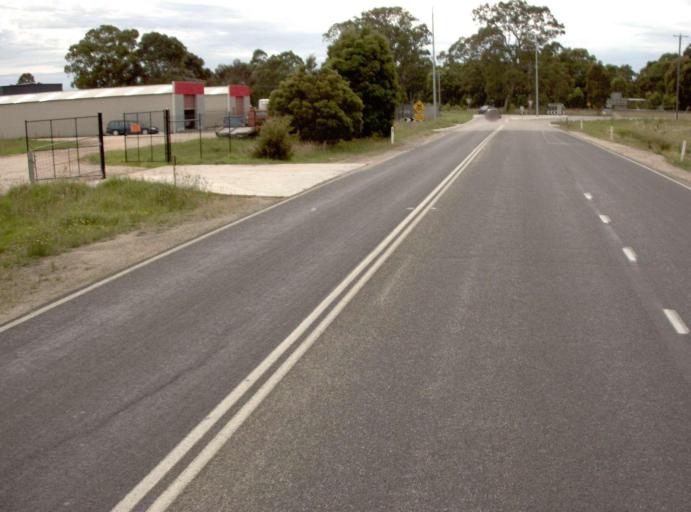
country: AU
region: Victoria
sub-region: East Gippsland
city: Bairnsdale
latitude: -37.8432
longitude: 147.5872
